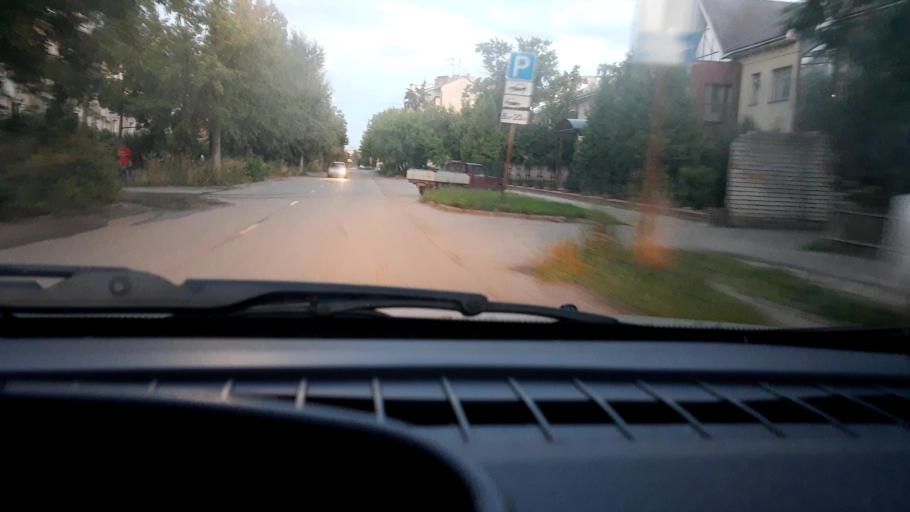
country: RU
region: Nizjnij Novgorod
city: Dzerzhinsk
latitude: 56.2409
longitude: 43.4789
